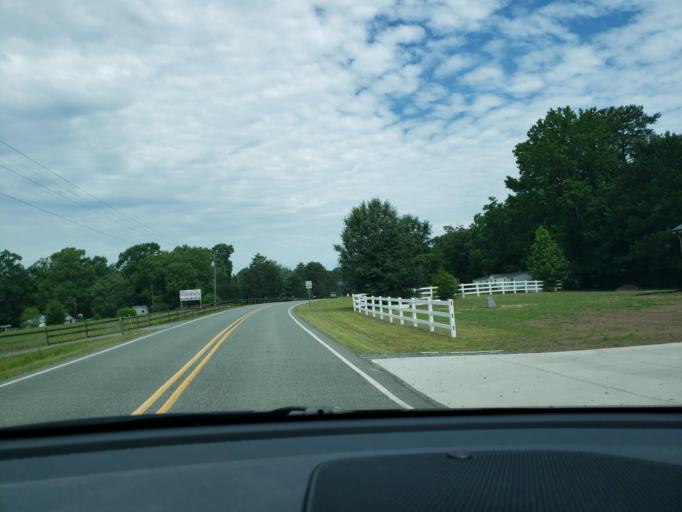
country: US
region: North Carolina
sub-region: Wake County
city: Green Level
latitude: 35.7915
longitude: -78.9710
